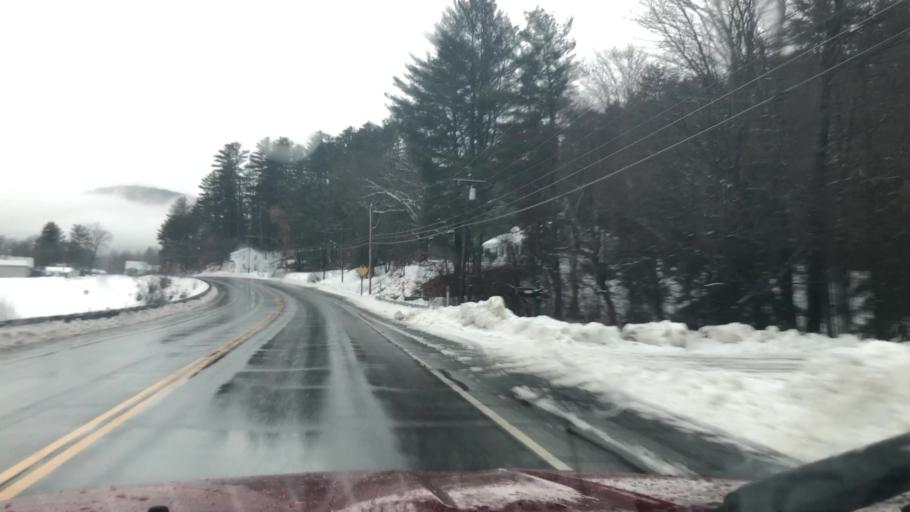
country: US
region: Maine
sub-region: Oxford County
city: Rumford
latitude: 44.4994
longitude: -70.6658
